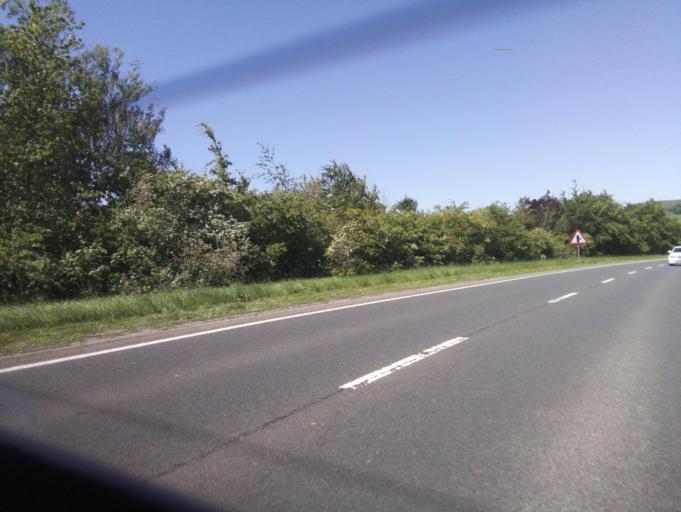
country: GB
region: Scotland
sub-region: The Scottish Borders
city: Selkirk
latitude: 55.4852
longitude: -2.8342
